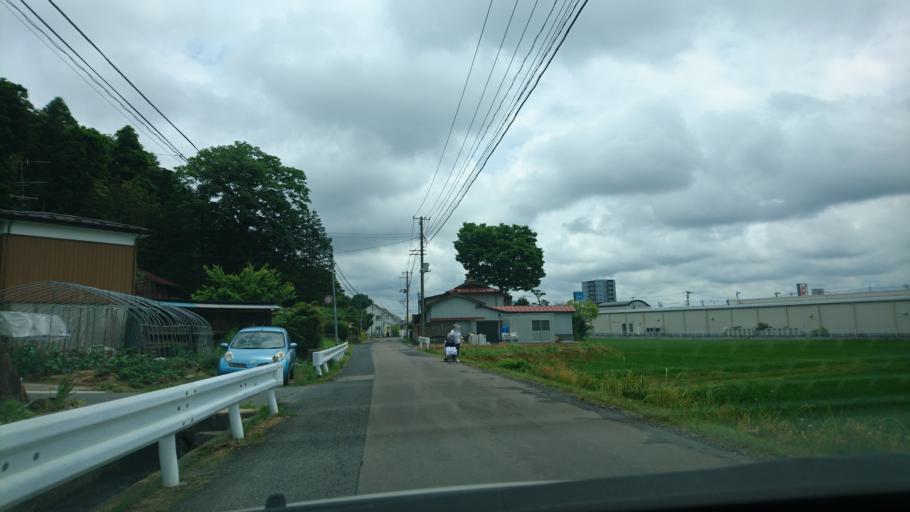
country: JP
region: Iwate
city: Ichinoseki
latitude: 38.9405
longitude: 141.1073
